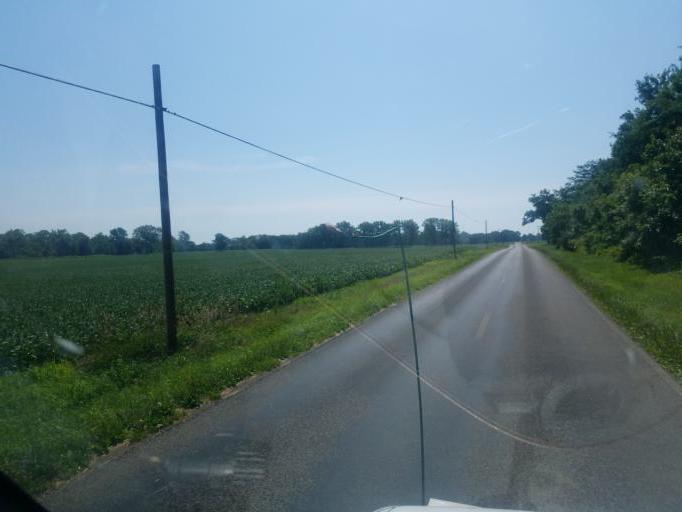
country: US
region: Ohio
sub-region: Champaign County
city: North Lewisburg
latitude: 40.2104
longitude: -83.4982
